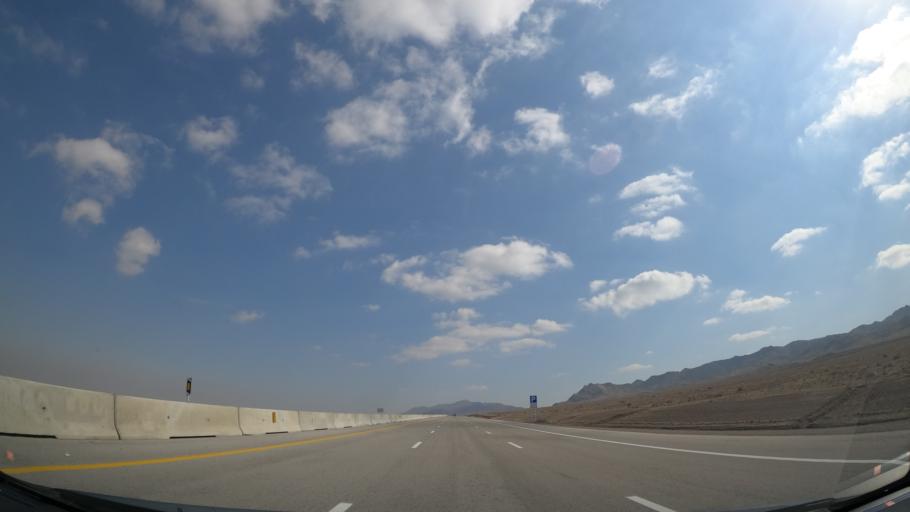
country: IR
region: Alborz
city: Eshtehard
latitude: 35.7123
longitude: 50.5909
